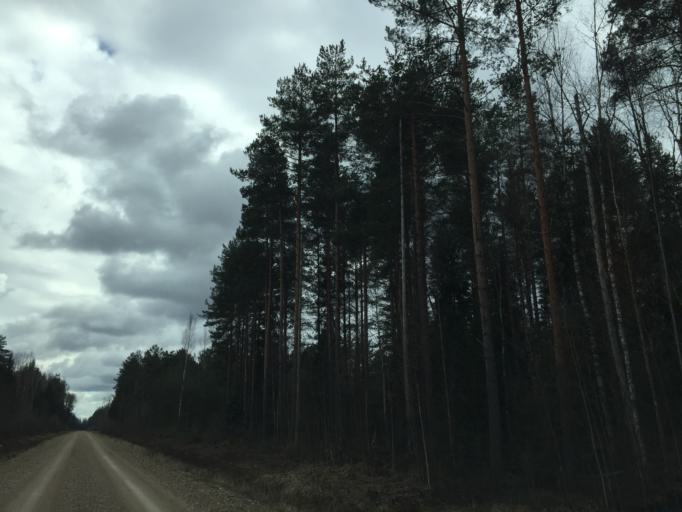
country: LV
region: Akniste
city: Akniste
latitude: 56.0906
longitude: 25.7617
